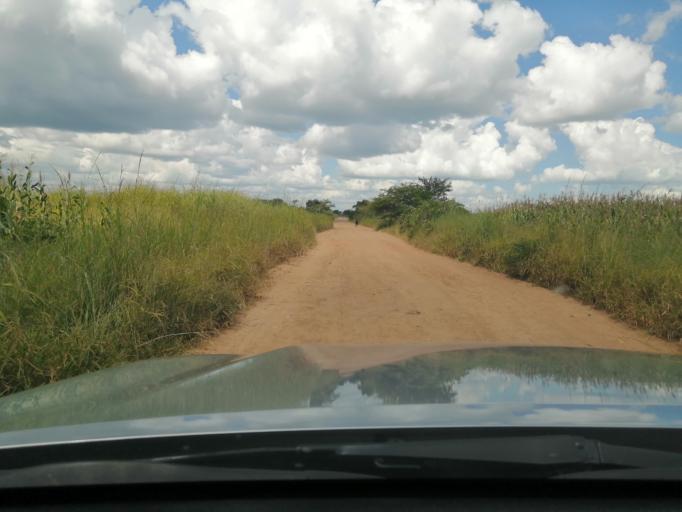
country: ZM
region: Lusaka
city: Lusaka
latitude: -15.1984
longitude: 28.0040
